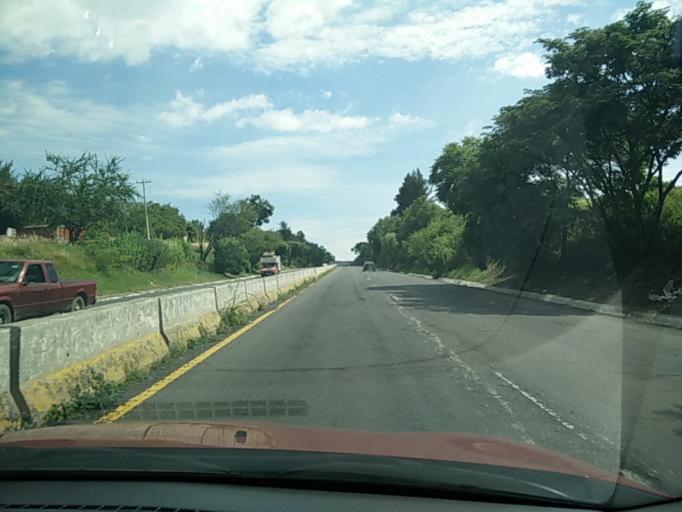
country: MX
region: Jalisco
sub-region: Ixtlahuacan de los Membrillos
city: Los Cedros
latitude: 20.3764
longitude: -103.2160
